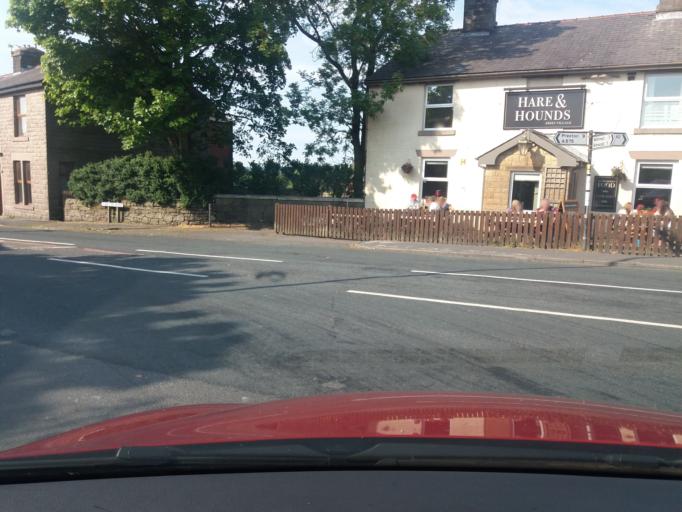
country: GB
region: England
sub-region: Blackburn with Darwen
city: Darwen
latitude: 53.6967
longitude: -2.5424
